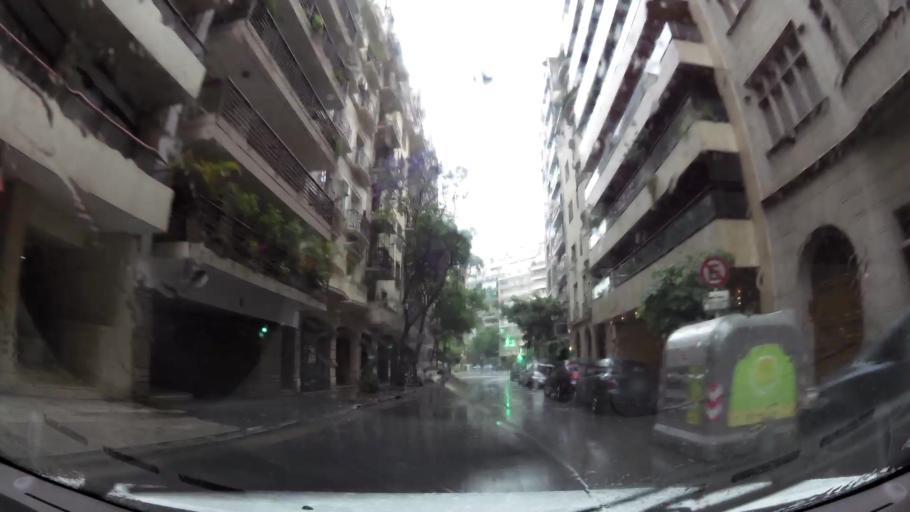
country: AR
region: Buenos Aires F.D.
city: Retiro
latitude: -34.5928
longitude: -58.3880
